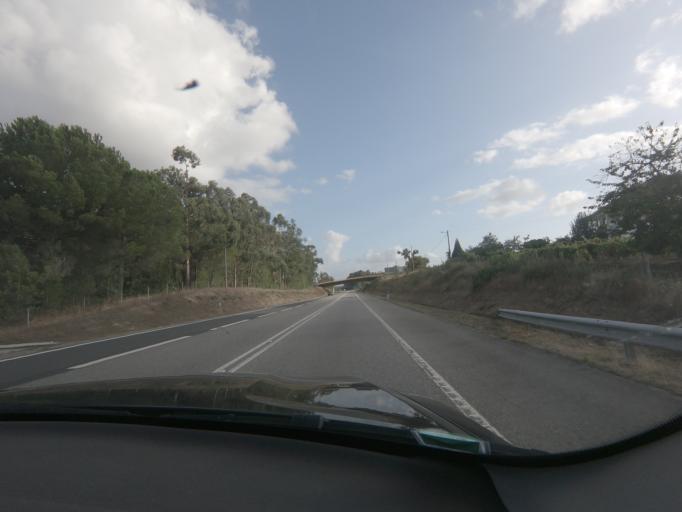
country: PT
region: Viseu
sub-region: Concelho de Tondela
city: Tondela
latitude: 40.5497
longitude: -8.0533
